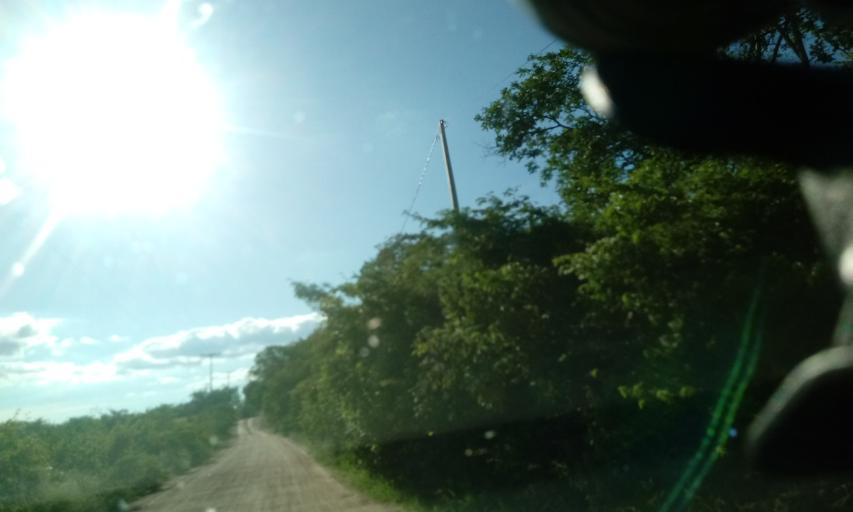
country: BR
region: Bahia
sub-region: Riacho De Santana
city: Riacho de Santana
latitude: -13.8000
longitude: -42.7397
